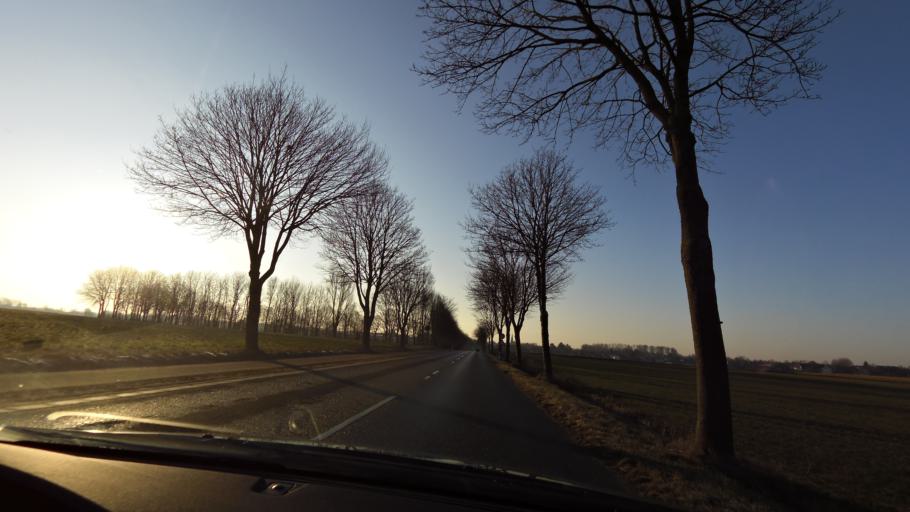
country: NL
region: Limburg
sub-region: Gemeente Kerkrade
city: Kerkrade
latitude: 50.8234
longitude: 6.0535
